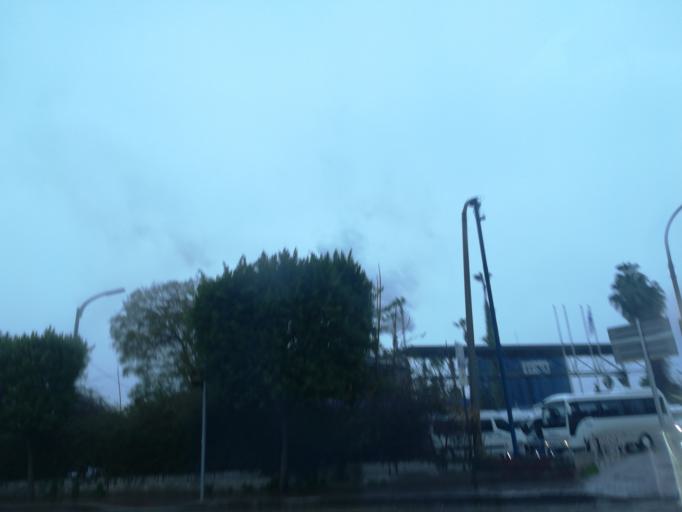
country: TR
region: Adana
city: Seyhan
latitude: 36.9943
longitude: 35.3094
